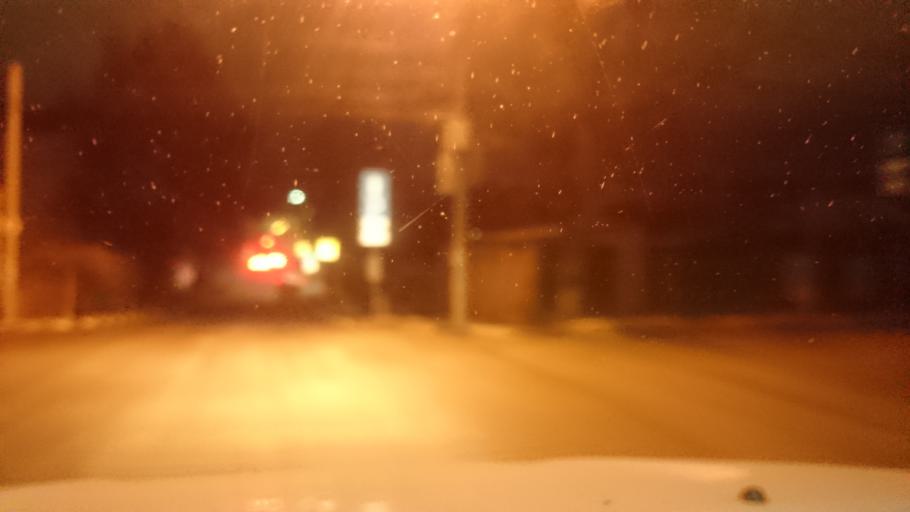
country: RU
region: Tula
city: Tula
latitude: 54.1858
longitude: 37.6152
